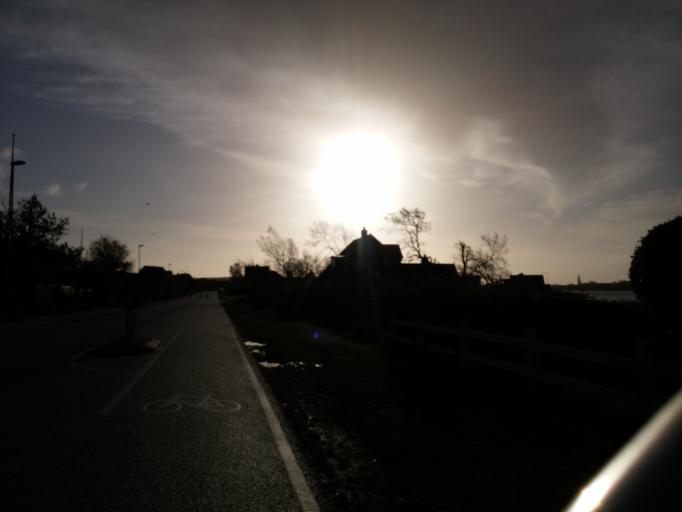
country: DK
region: South Denmark
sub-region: Kerteminde Kommune
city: Kerteminde
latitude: 55.4511
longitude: 10.6479
